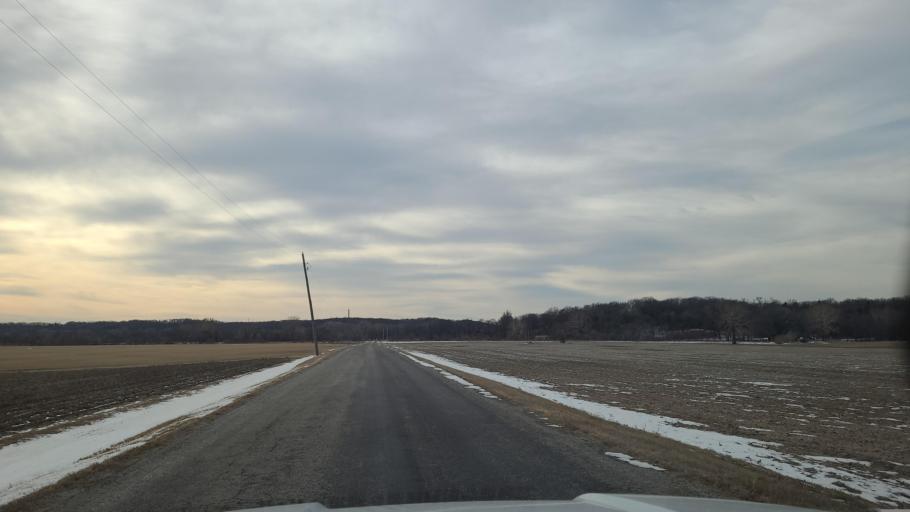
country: US
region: Kansas
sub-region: Douglas County
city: Lawrence
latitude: 39.0283
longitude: -95.3121
